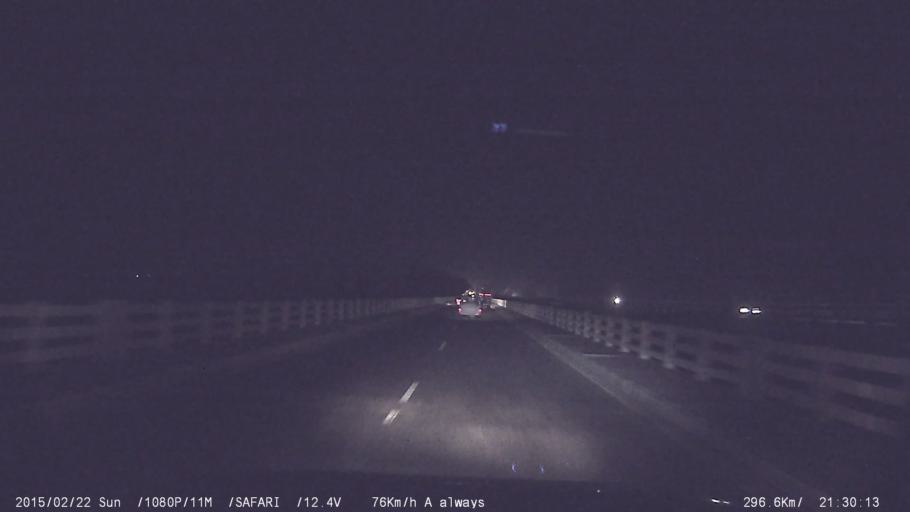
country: IN
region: Tamil Nadu
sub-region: Karur
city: Karur
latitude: 10.9429
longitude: 78.0572
